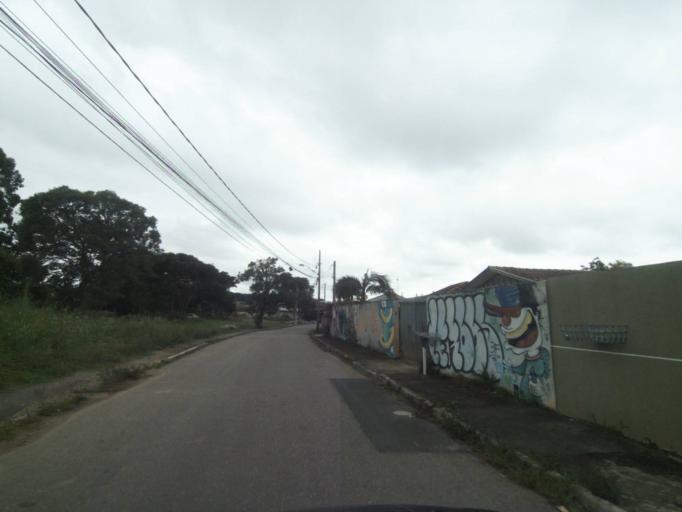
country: BR
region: Parana
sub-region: Curitiba
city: Curitiba
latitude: -25.4675
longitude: -49.3215
